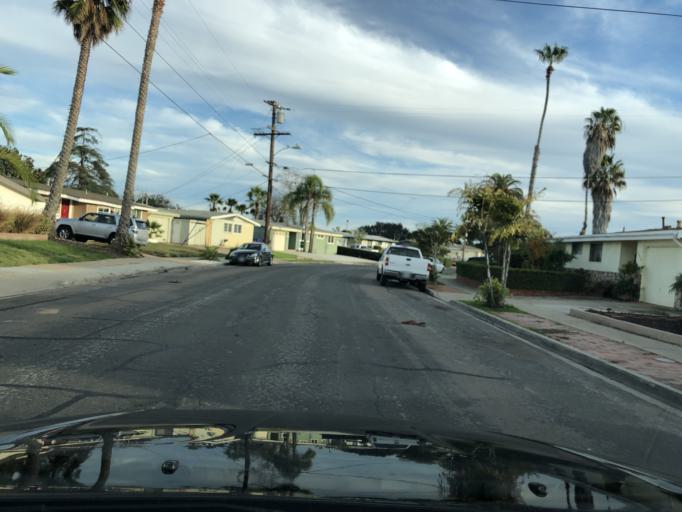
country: US
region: California
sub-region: San Diego County
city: La Jolla
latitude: 32.8330
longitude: -117.1915
